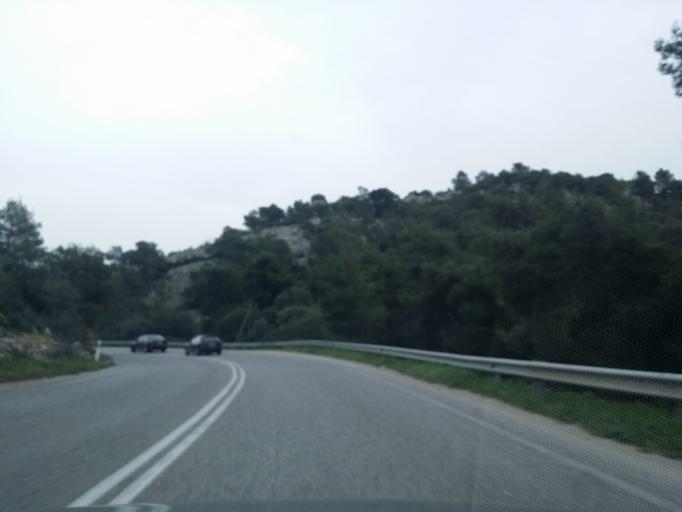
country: GR
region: Attica
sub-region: Nomarchia Dytikis Attikis
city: Mandra
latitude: 38.0957
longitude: 23.4673
